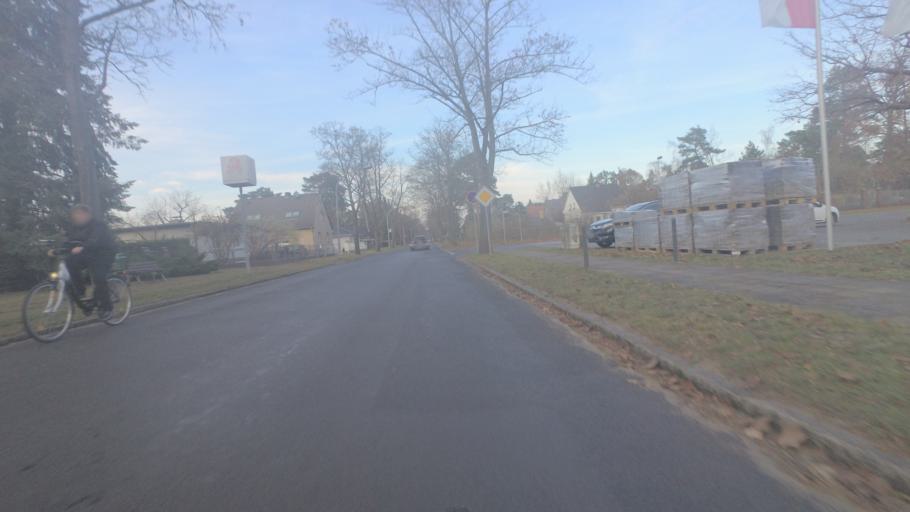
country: DE
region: Brandenburg
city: Am Mellensee
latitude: 52.1694
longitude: 13.4018
